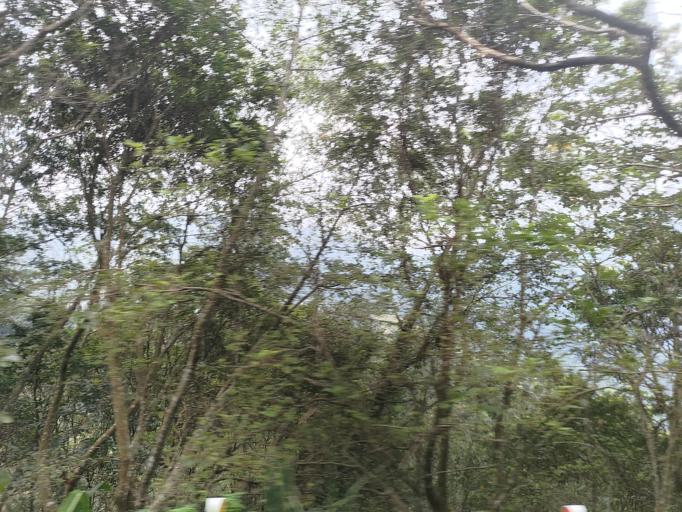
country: TW
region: Taiwan
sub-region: Hsinchu
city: Hsinchu
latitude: 24.6188
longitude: 121.0928
